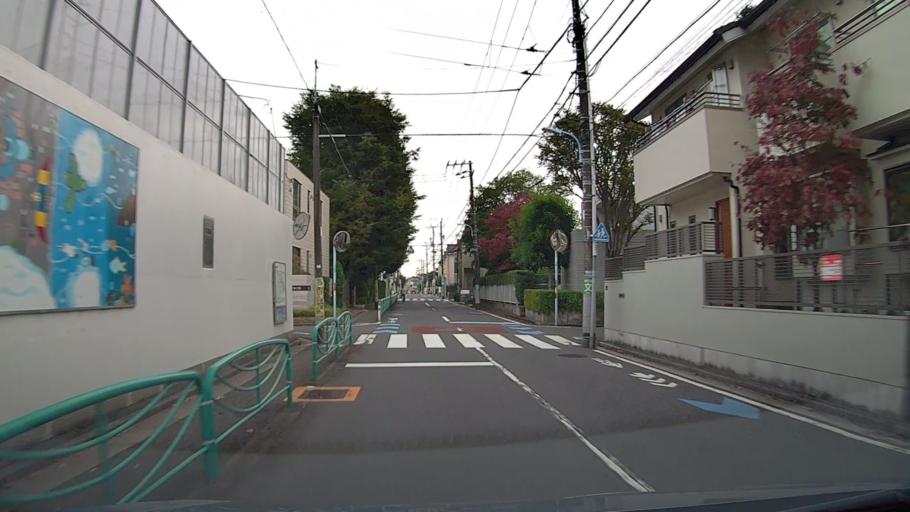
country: JP
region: Tokyo
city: Musashino
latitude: 35.7005
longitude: 139.6085
